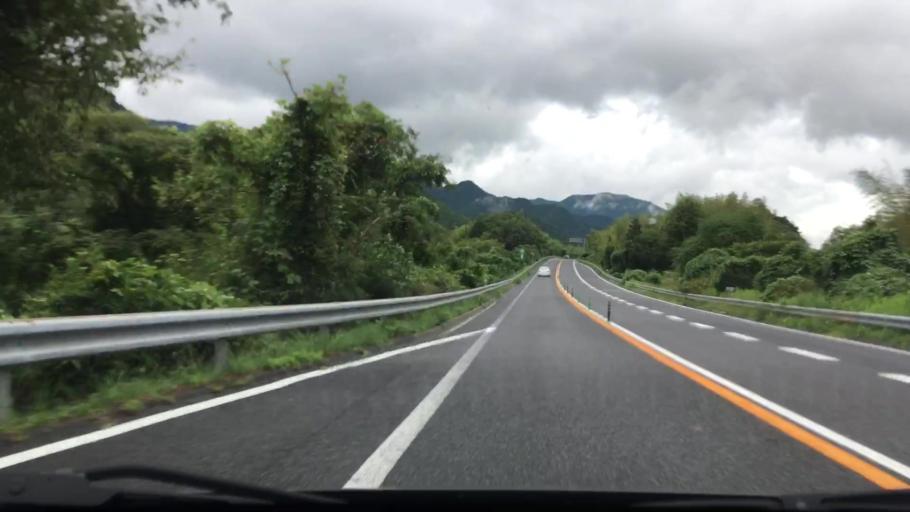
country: JP
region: Hyogo
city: Nishiwaki
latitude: 35.0901
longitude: 134.7772
